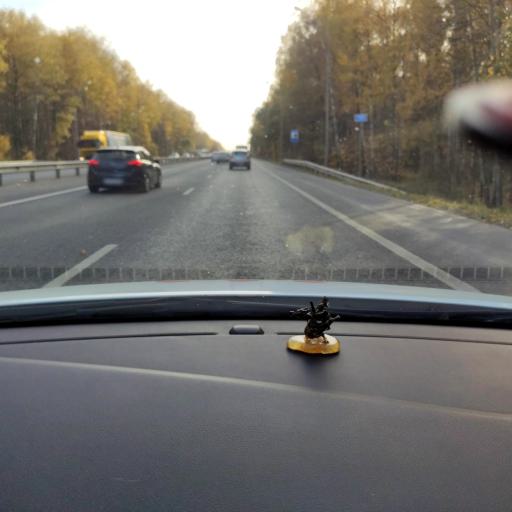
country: RU
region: Tatarstan
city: Osinovo
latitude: 55.8429
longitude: 48.8517
